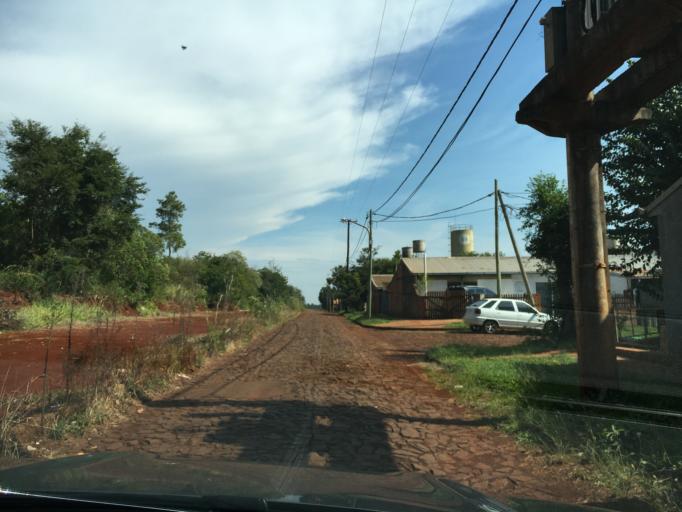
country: AR
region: Misiones
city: Puerto Rico
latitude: -26.8047
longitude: -55.0027
